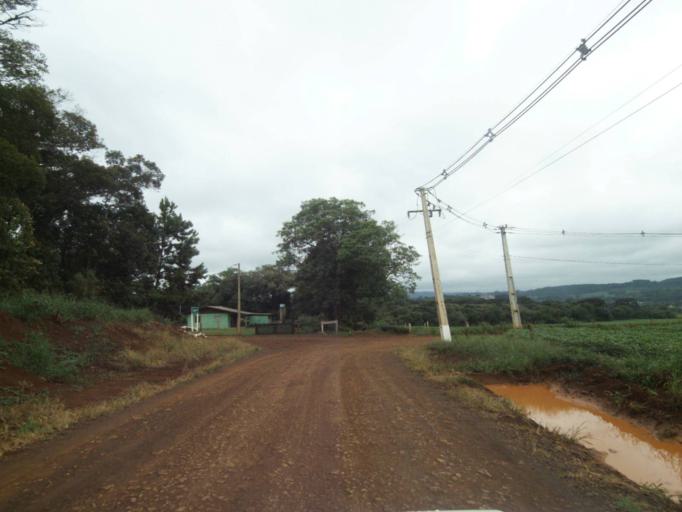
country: BR
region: Parana
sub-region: Pitanga
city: Pitanga
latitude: -24.9414
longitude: -51.8798
